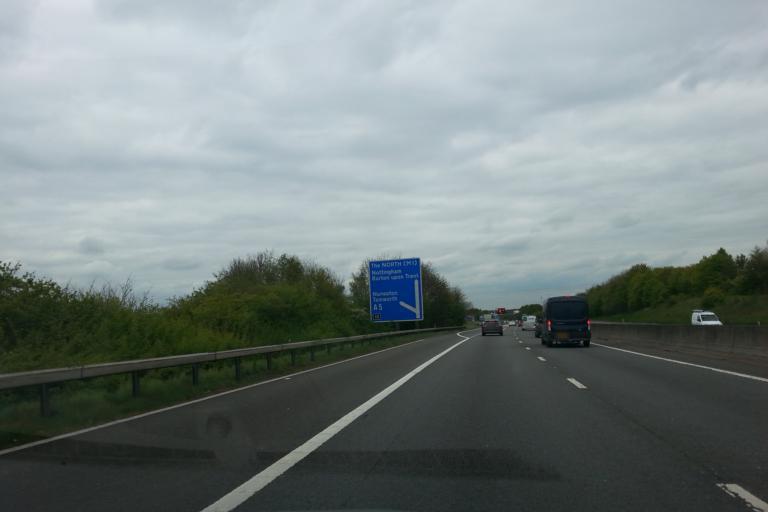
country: GB
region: England
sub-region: Warwickshire
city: Kingsbury
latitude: 52.5979
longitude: -1.6491
